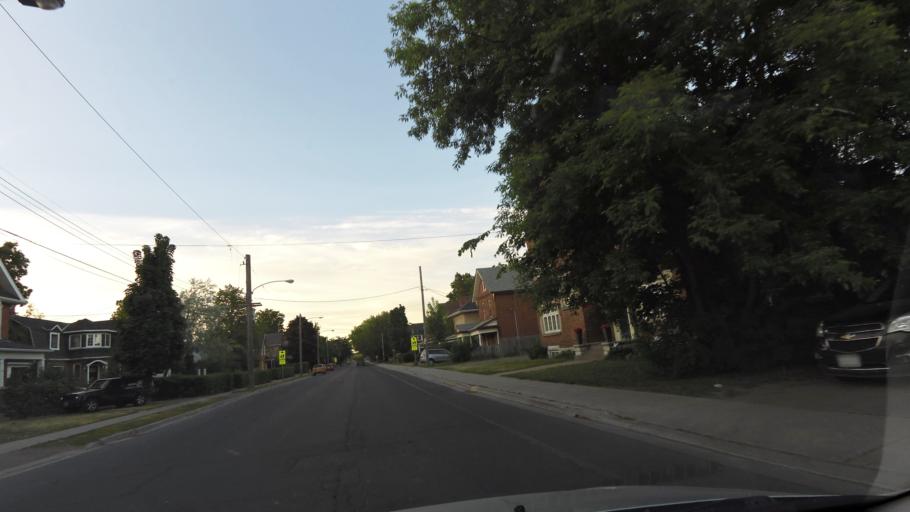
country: CA
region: Ontario
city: Peterborough
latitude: 44.3168
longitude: -78.3192
